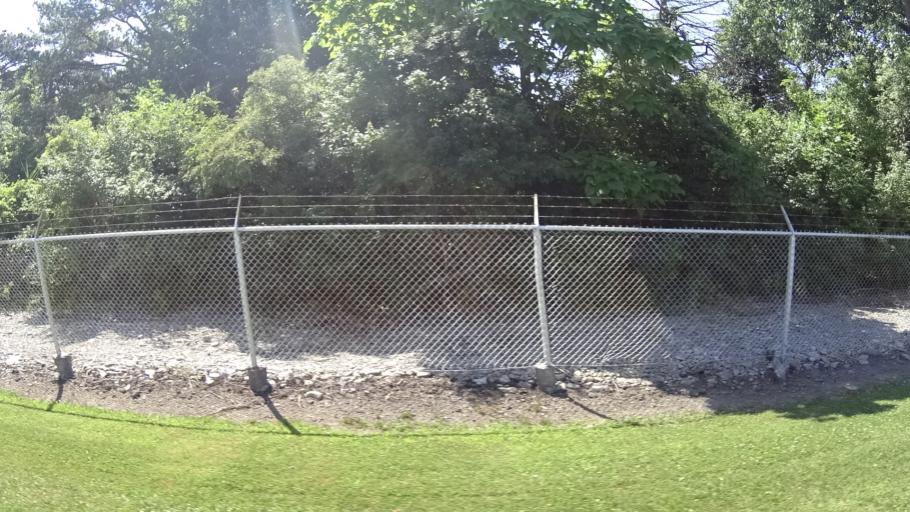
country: US
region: Ohio
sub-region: Erie County
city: Sandusky
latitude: 41.4175
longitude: -82.8094
